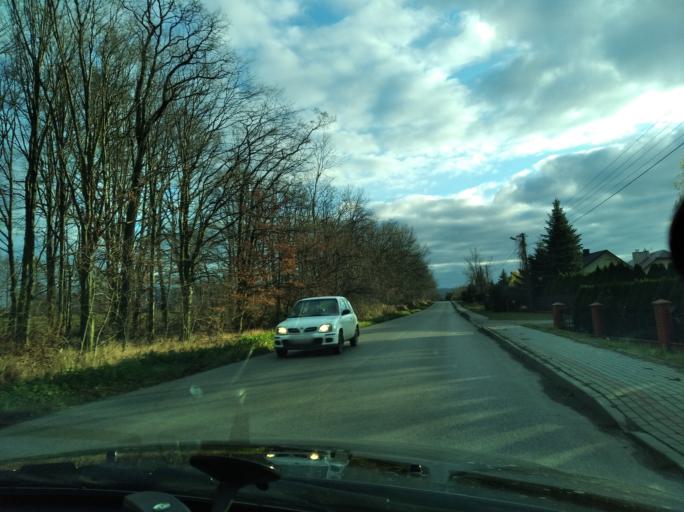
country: PL
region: Subcarpathian Voivodeship
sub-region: Powiat rzeszowski
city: Krasne
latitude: 50.0521
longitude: 22.1222
